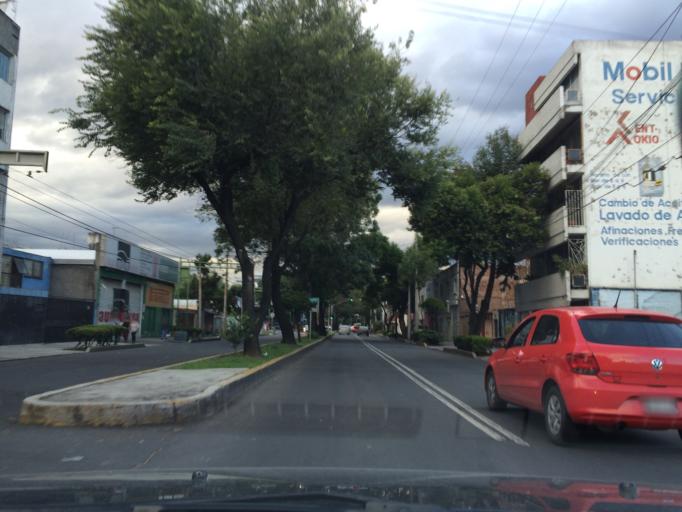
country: MX
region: Mexico City
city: Coyoacan
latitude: 19.3660
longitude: -99.1532
